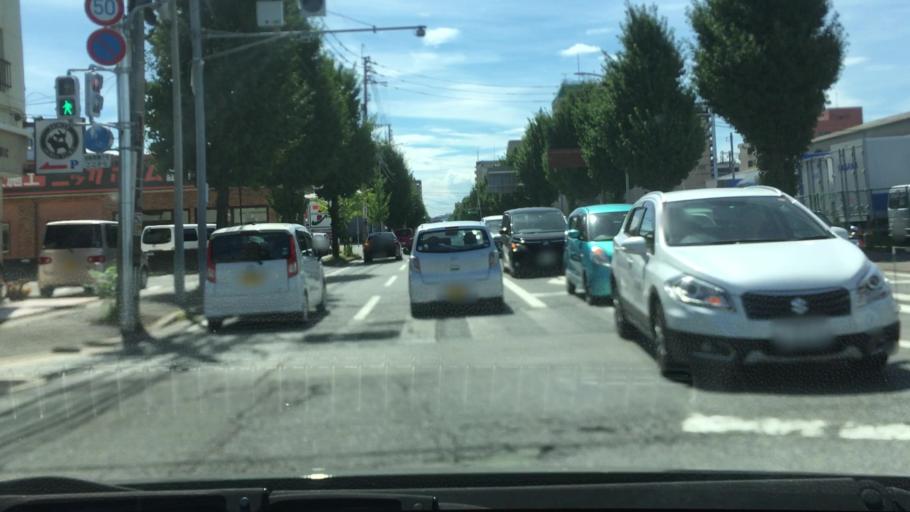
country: JP
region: Fukuoka
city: Fukuoka-shi
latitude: 33.5719
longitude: 130.4230
